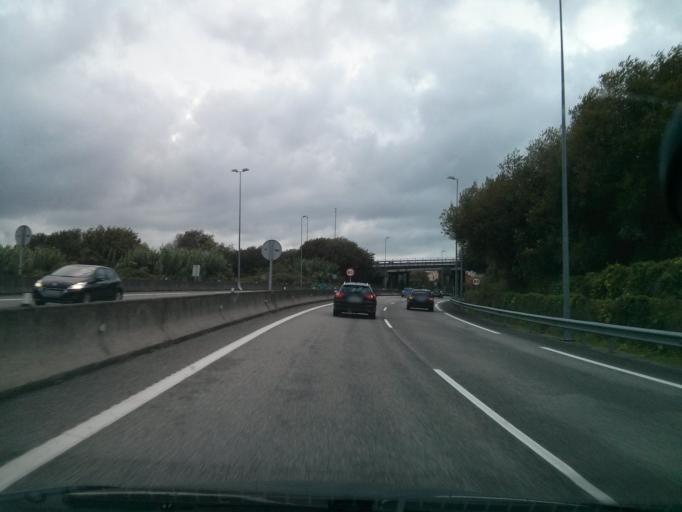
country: ES
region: Galicia
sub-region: Provincia de Pontevedra
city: Vigo
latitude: 42.2072
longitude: -8.6944
